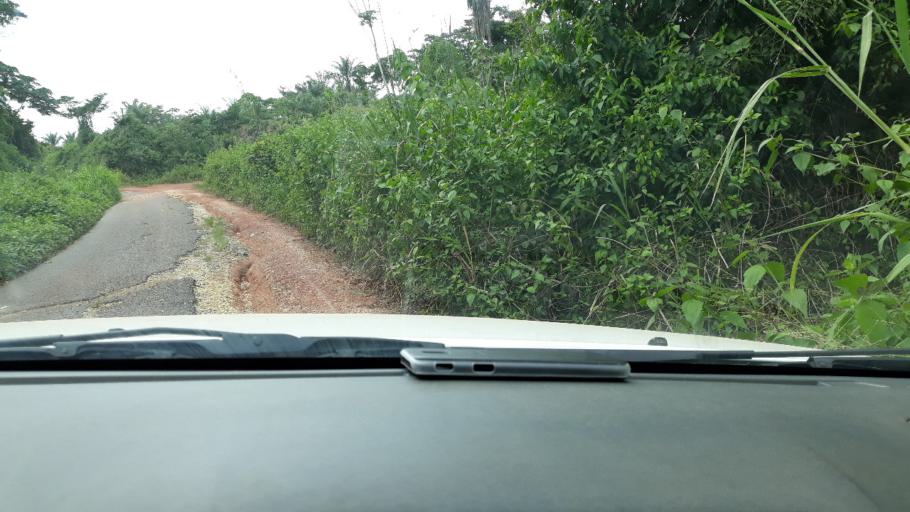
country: CD
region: Maniema
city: Kindu
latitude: -2.7874
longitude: 26.1746
